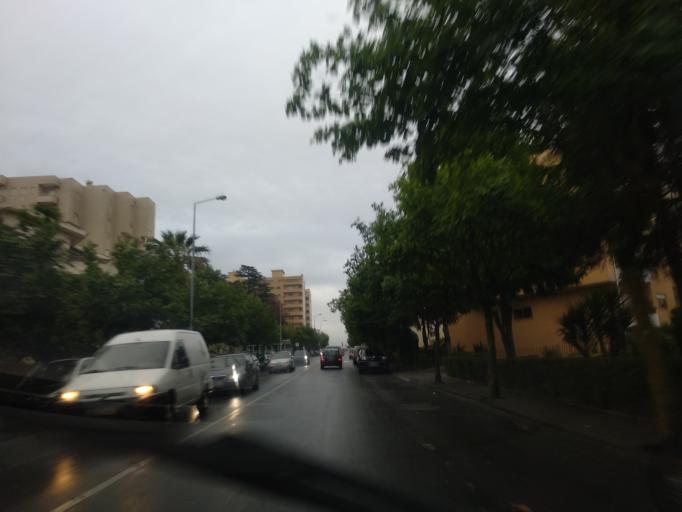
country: PT
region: Porto
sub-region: Gondomar
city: Rio Tinto
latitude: 41.1765
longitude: -8.5584
